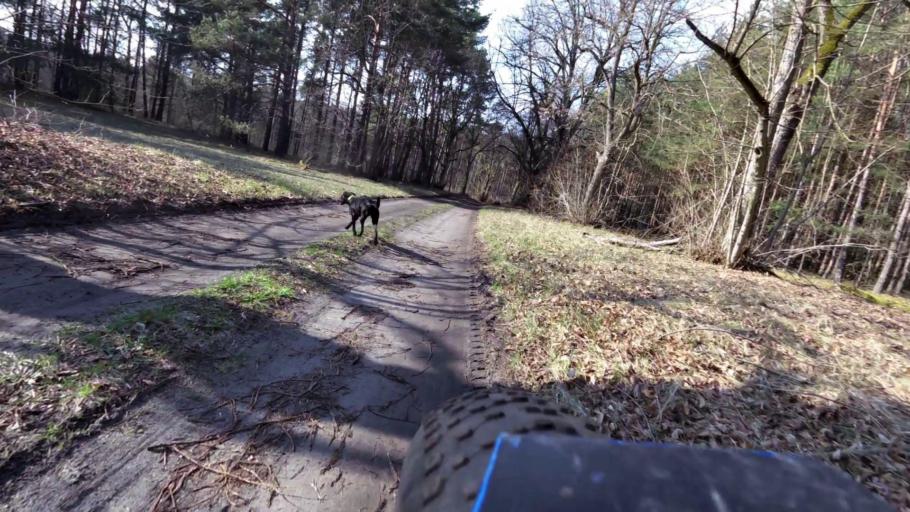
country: PL
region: Lubusz
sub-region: Powiat slubicki
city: Cybinka
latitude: 52.2405
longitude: 14.7800
